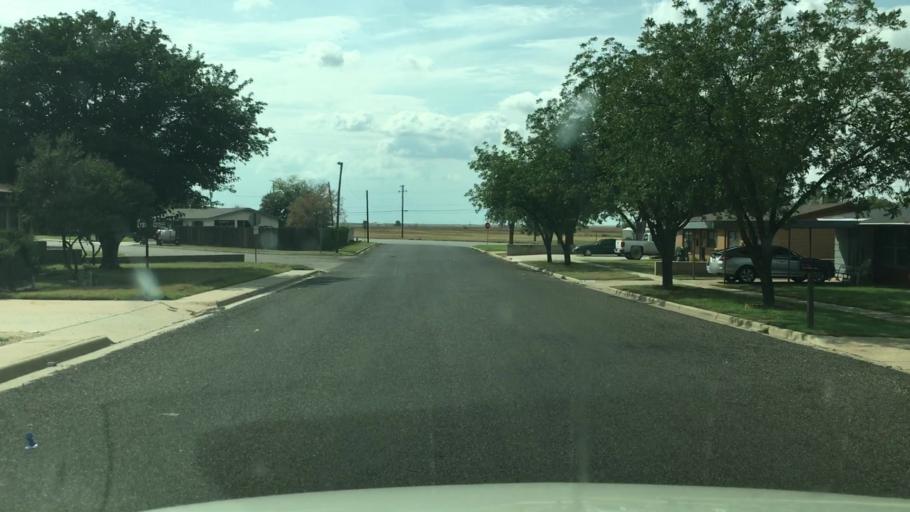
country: US
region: Texas
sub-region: Dawson County
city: Lamesa
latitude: 32.7530
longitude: -101.9557
